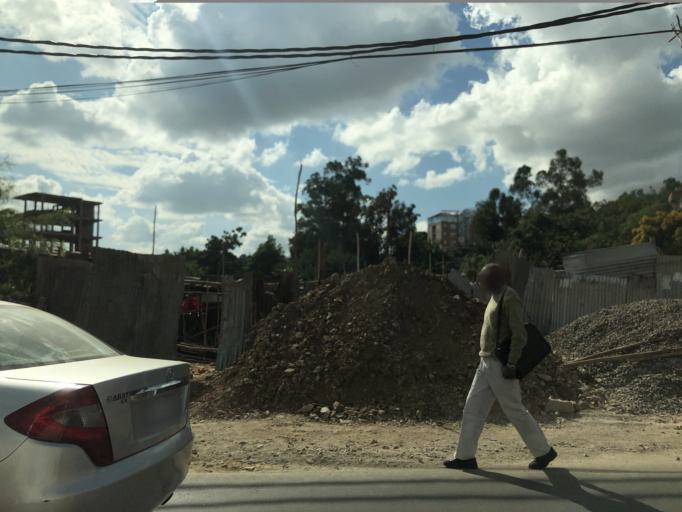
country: ET
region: Adis Abeba
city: Addis Ababa
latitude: 9.0316
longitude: 38.7736
